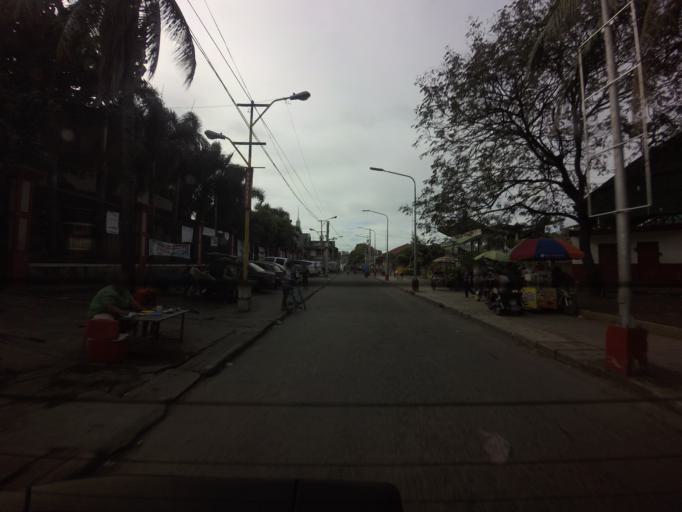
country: PH
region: Metro Manila
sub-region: Caloocan City
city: Niugan
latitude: 14.6495
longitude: 120.9569
